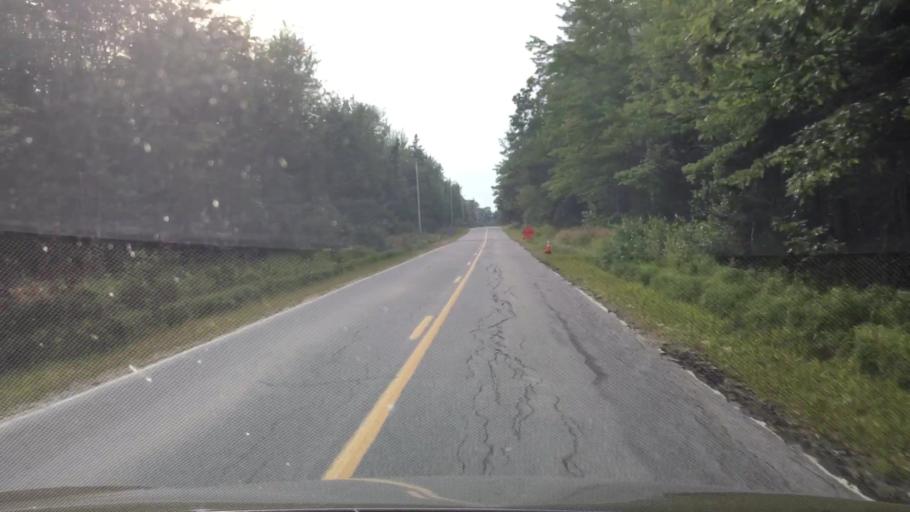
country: US
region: Maine
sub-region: Hancock County
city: Penobscot
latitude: 44.4733
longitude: -68.7713
